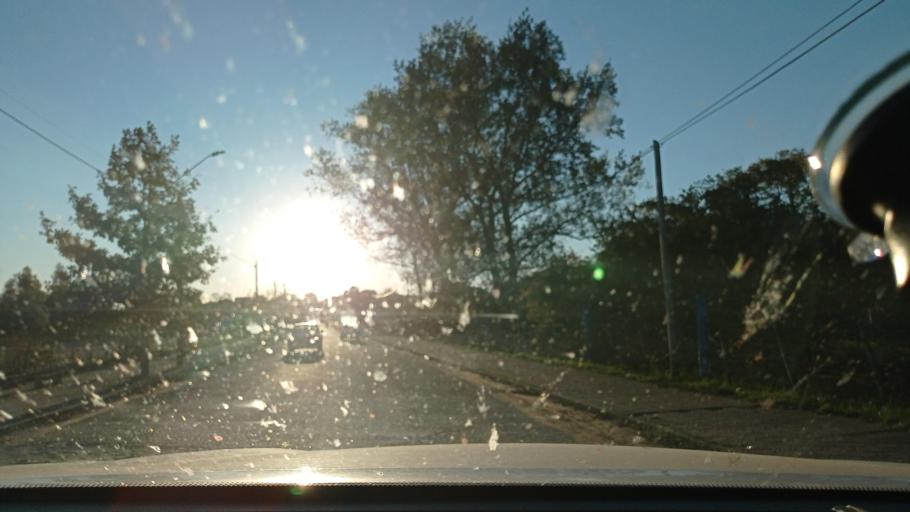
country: UY
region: Florida
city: Florida
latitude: -34.0924
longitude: -56.2244
